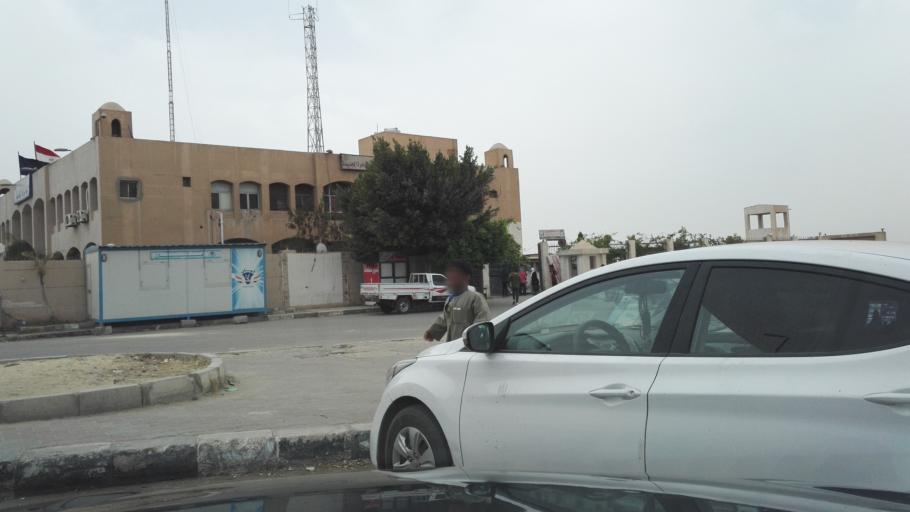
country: EG
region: Muhafazat al Qahirah
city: Halwan
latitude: 29.9823
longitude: 31.4209
